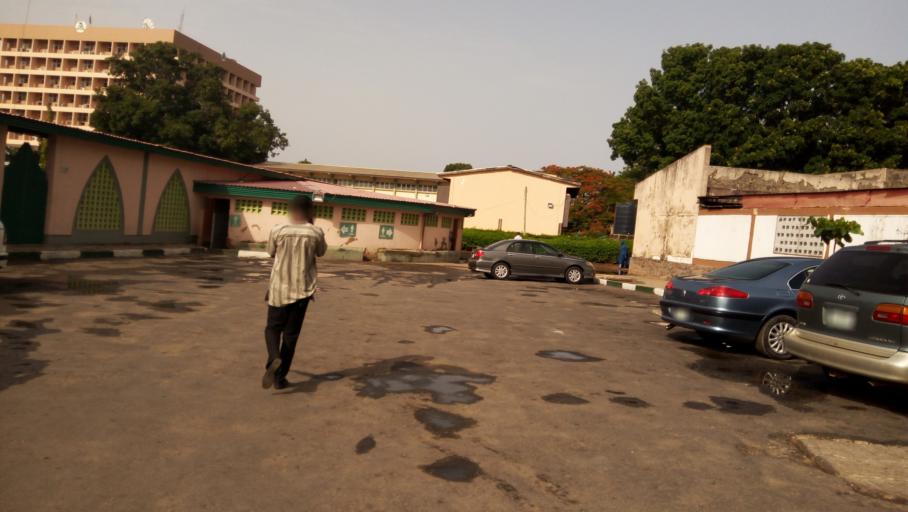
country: NG
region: Kaduna
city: Zaria
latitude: 11.1520
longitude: 7.6551
